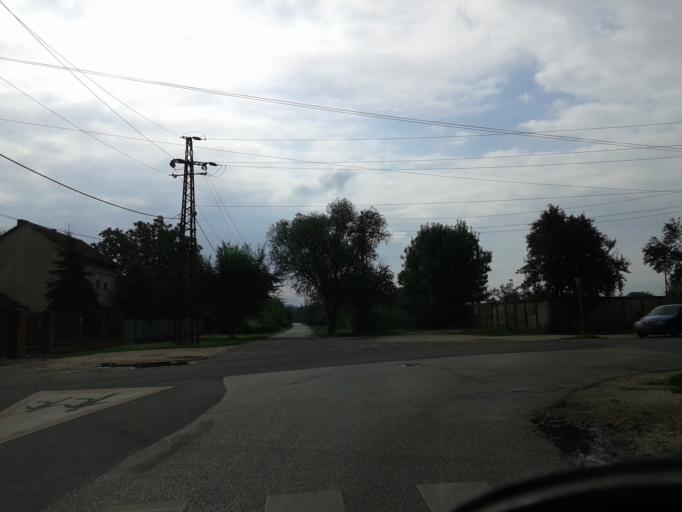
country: HU
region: Csongrad
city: Szeged
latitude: 46.2733
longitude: 20.1229
